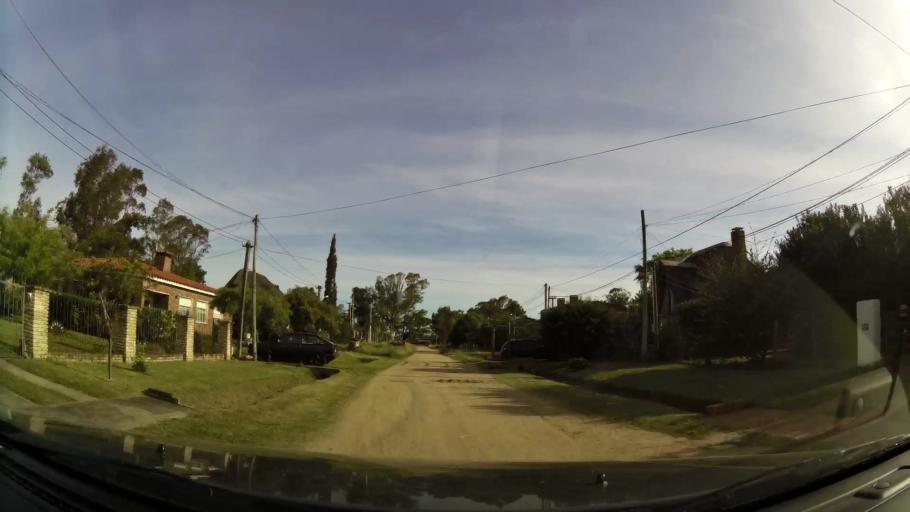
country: UY
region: Canelones
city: Atlantida
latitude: -34.7868
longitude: -55.8490
